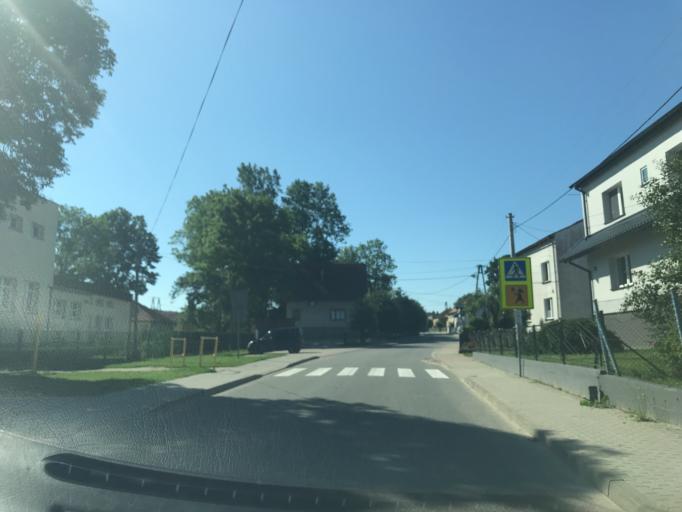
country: PL
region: Warmian-Masurian Voivodeship
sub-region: Powiat ostrodzki
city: Ostroda
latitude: 53.5740
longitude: 19.9209
